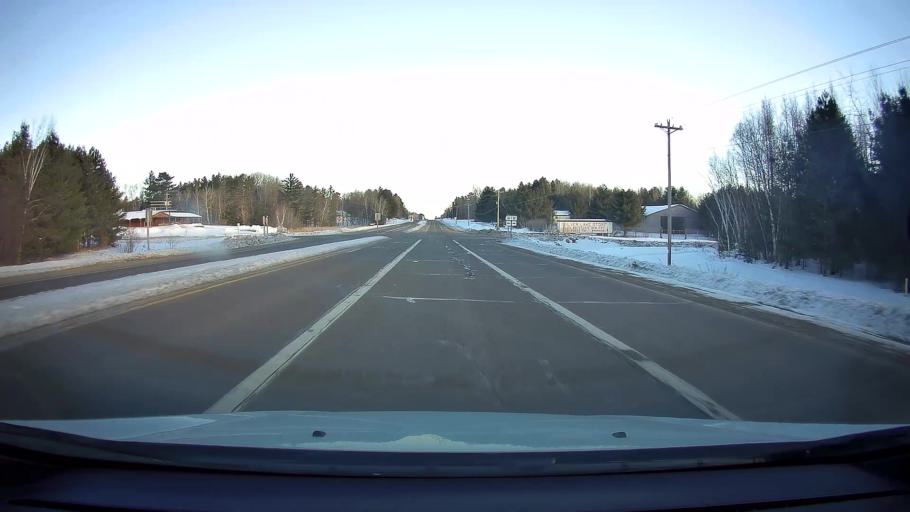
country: US
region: Wisconsin
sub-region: Barron County
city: Cumberland
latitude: 45.5576
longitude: -92.0171
